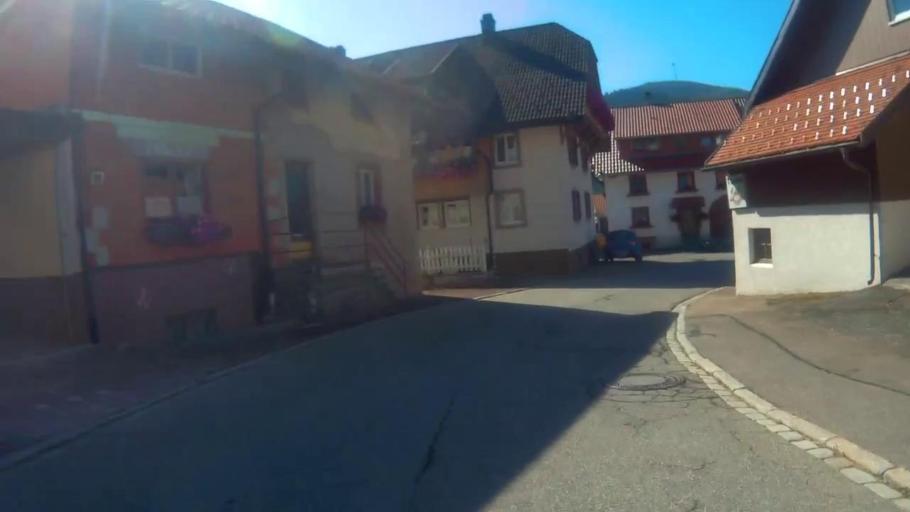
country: DE
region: Baden-Wuerttemberg
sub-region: Freiburg Region
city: Wembach
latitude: 47.7342
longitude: 7.9164
